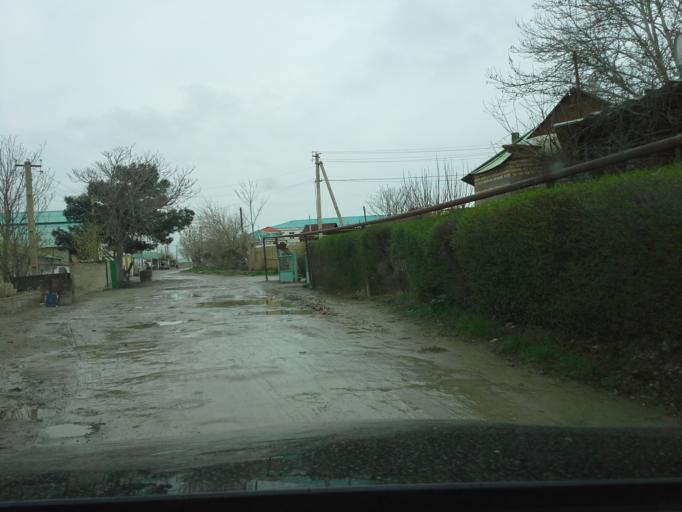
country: TM
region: Ahal
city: Abadan
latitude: 37.9603
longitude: 58.2067
